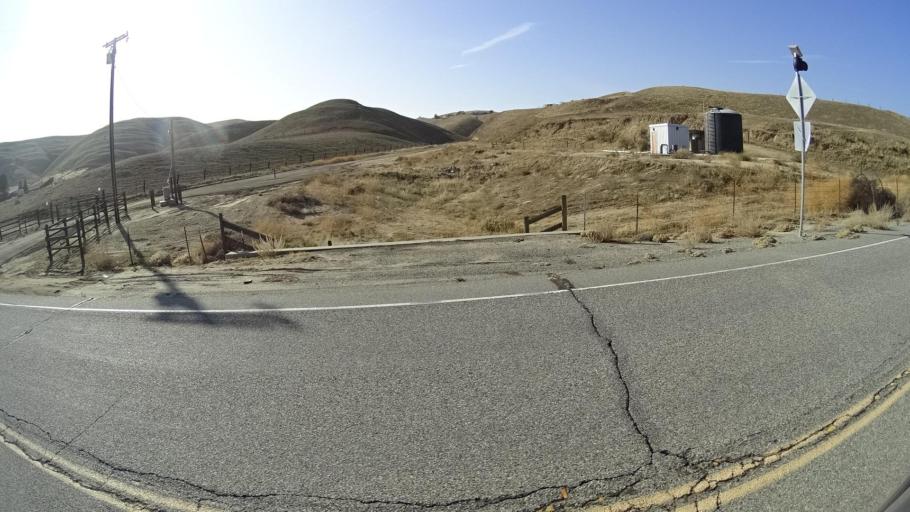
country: US
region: California
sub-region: Kern County
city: Oildale
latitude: 35.5277
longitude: -118.9721
